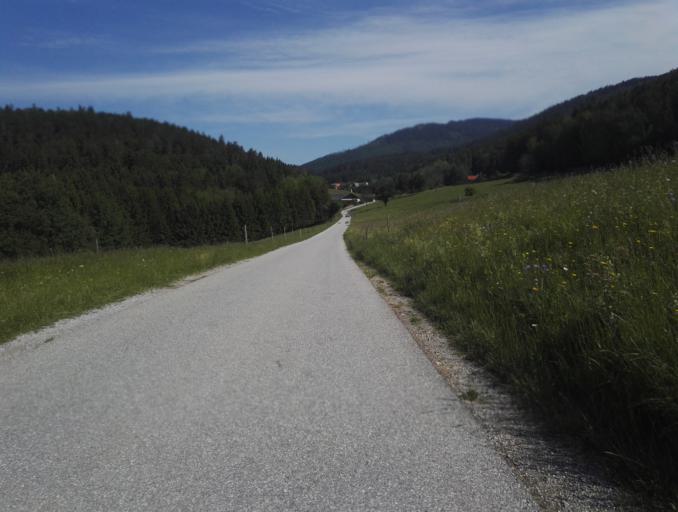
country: AT
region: Styria
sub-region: Politischer Bezirk Graz-Umgebung
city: Stattegg
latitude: 47.1527
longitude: 15.4342
